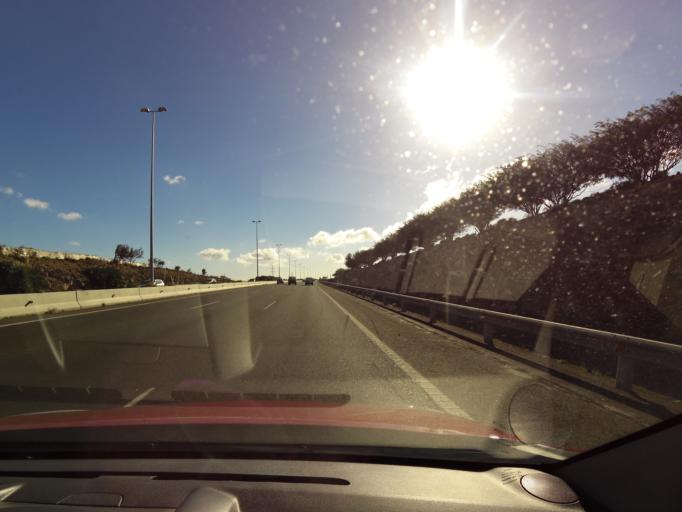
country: ES
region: Canary Islands
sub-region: Provincia de Las Palmas
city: Cruce de Arinaga
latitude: 27.8870
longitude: -15.4095
